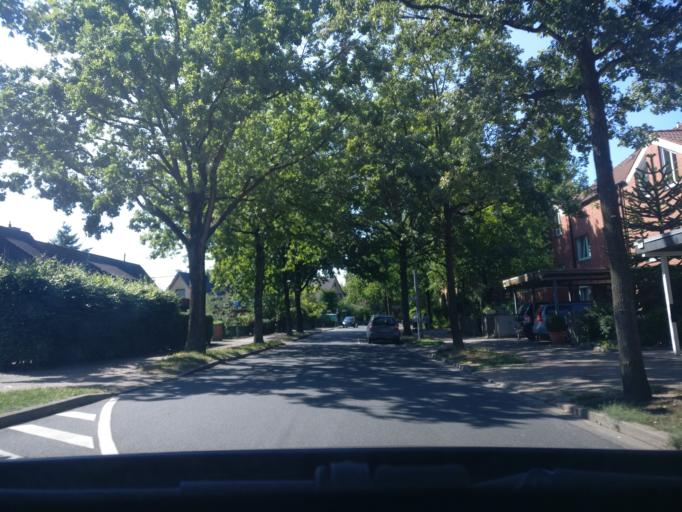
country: DE
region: Schleswig-Holstein
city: Norderstedt
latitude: 53.7018
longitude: 9.9885
